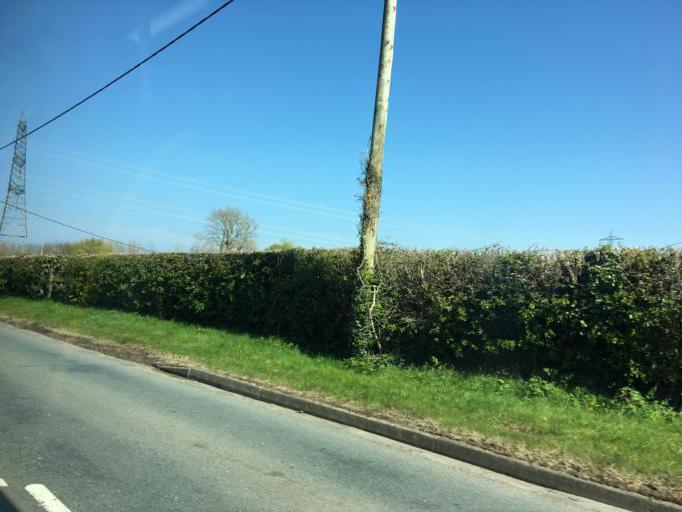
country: GB
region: Wales
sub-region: Anglesey
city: Menai Bridge
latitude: 53.2038
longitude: -4.1741
